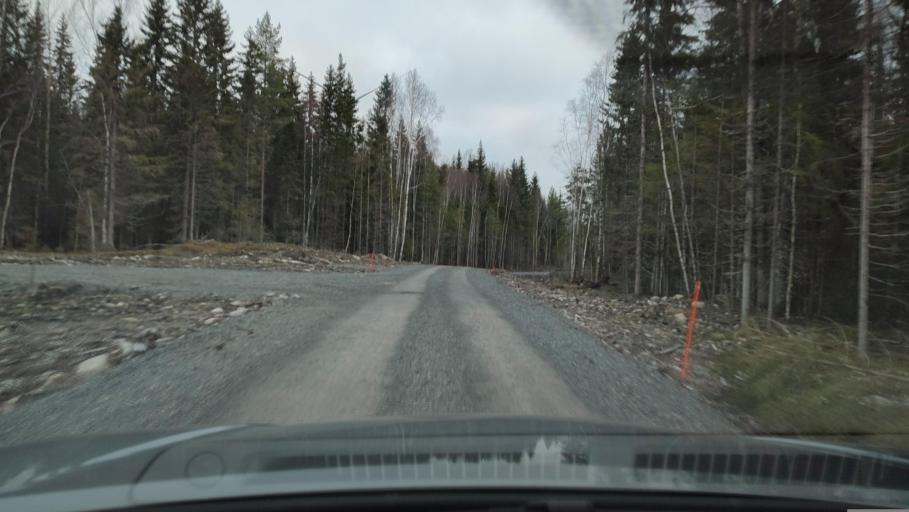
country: FI
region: Southern Ostrobothnia
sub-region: Suupohja
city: Karijoki
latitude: 62.1812
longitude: 21.5712
